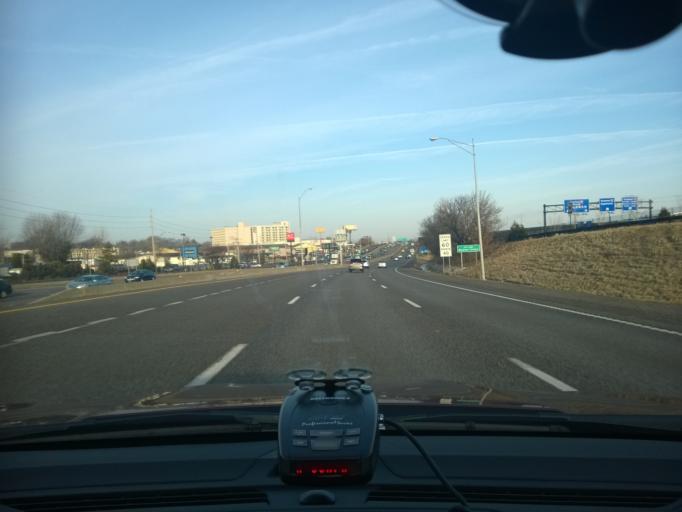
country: US
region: Missouri
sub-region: Saint Louis County
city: Woodson Terrace
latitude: 38.7342
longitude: -90.3533
